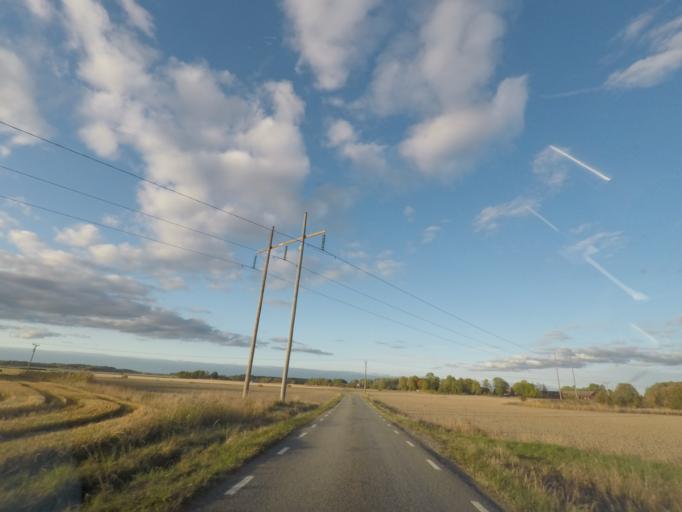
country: SE
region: Vaestmanland
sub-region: Kungsors Kommun
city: Kungsoer
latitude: 59.5193
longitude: 16.1137
